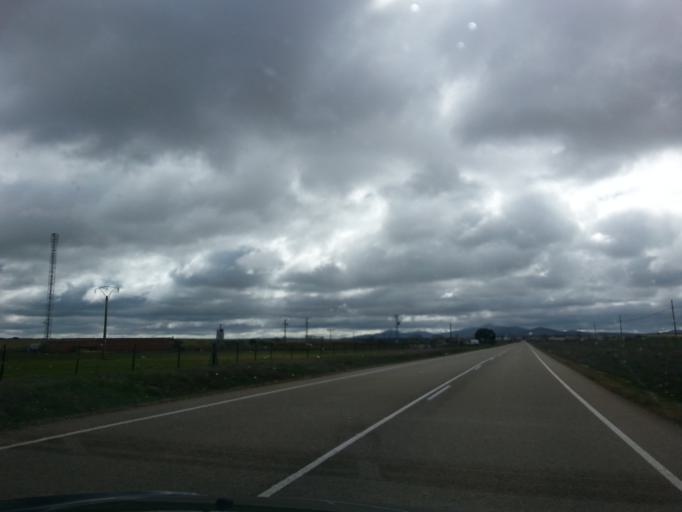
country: ES
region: Castille and Leon
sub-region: Provincia de Salamanca
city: Abusejo
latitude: 40.7226
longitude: -6.1514
